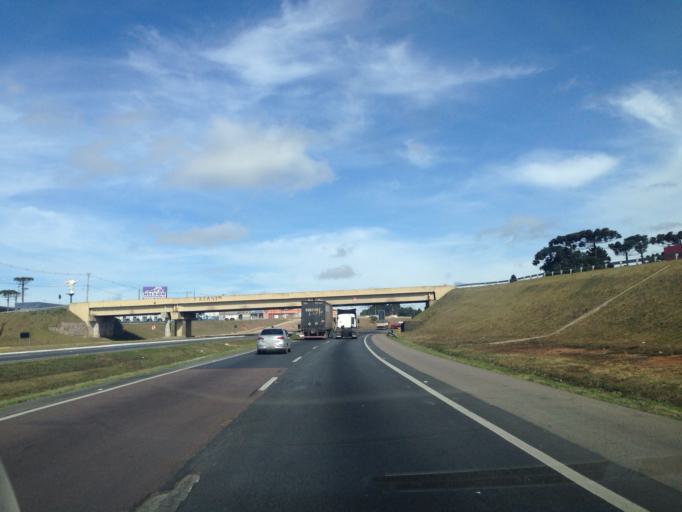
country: BR
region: Parana
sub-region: Sao Jose Dos Pinhais
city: Sao Jose dos Pinhais
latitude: -25.5591
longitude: -49.1508
